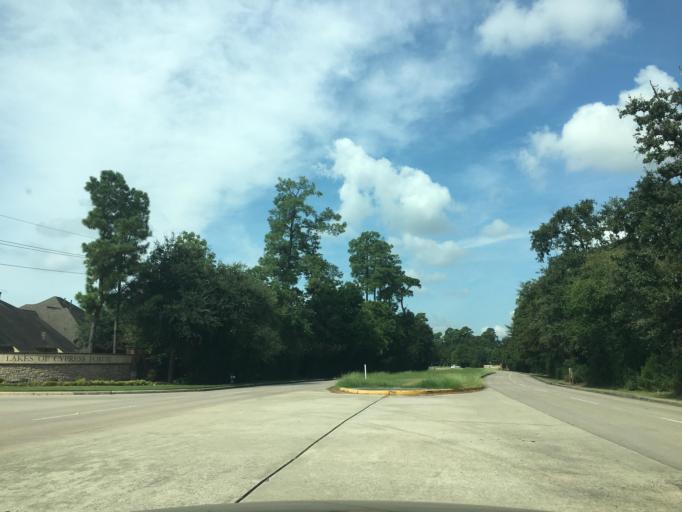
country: US
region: Texas
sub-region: Harris County
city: Spring
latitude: 30.0438
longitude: -95.4498
